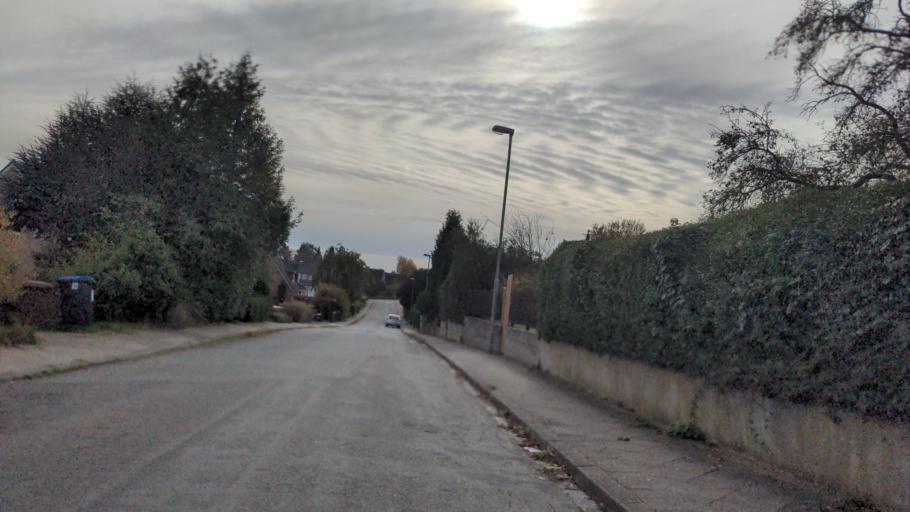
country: DE
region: Mecklenburg-Vorpommern
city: Selmsdorf
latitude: 53.9153
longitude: 10.8219
